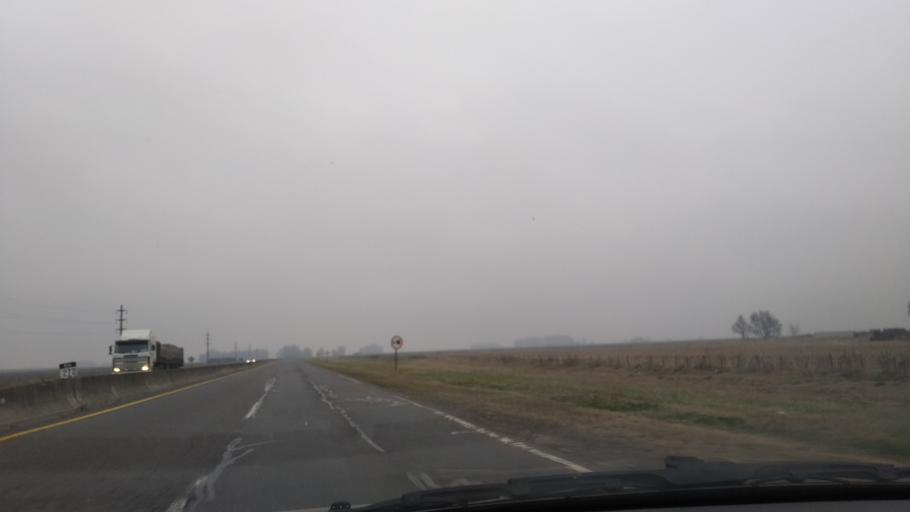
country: AR
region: Buenos Aires
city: Olavarria
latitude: -36.8574
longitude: -60.0885
